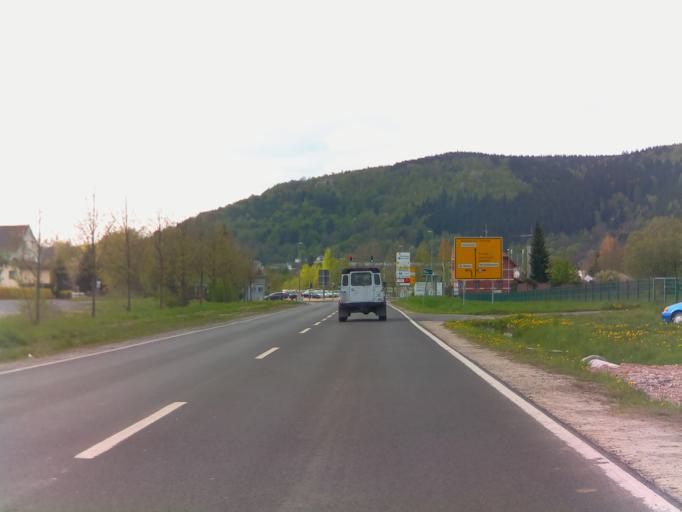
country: DE
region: Bavaria
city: Foritz
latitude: 50.3494
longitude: 11.2126
